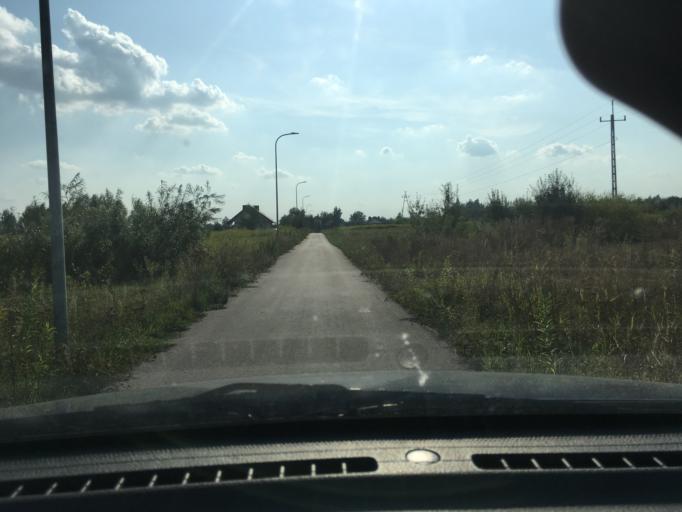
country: PL
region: Masovian Voivodeship
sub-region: Powiat piaseczynski
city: Lesznowola
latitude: 52.0534
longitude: 20.9362
